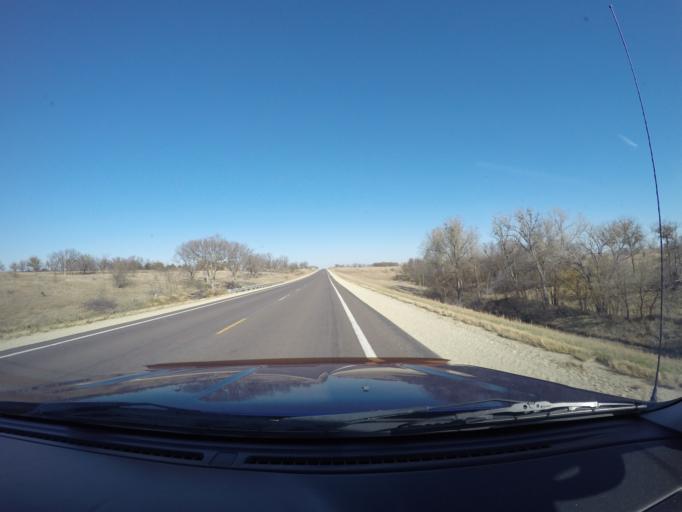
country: US
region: Kansas
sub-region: Marshall County
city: Blue Rapids
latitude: 39.6625
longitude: -96.7505
